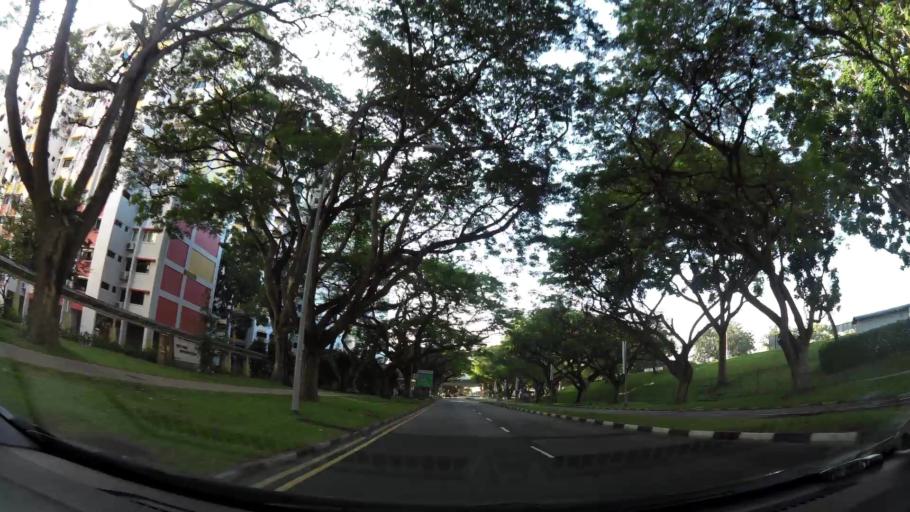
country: SG
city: Singapore
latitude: 1.3274
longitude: 103.9401
